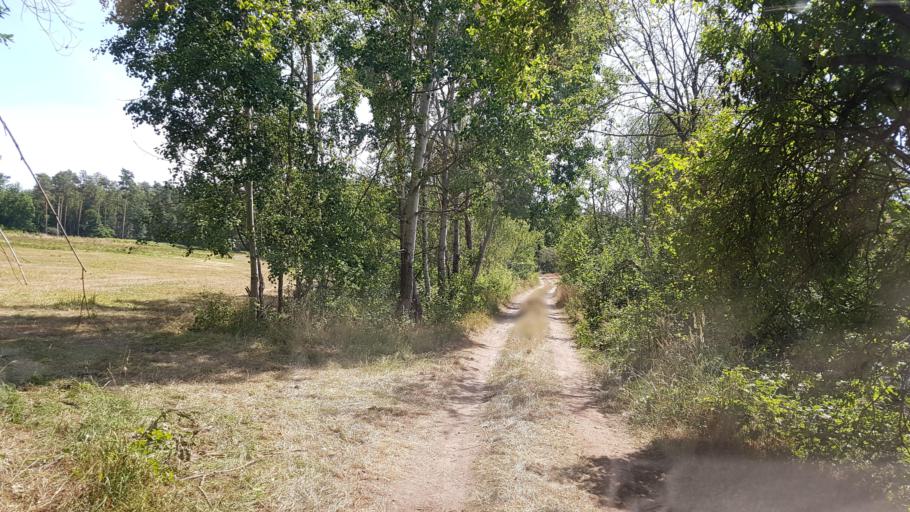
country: DE
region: Brandenburg
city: Finsterwalde
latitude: 51.6657
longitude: 13.7585
